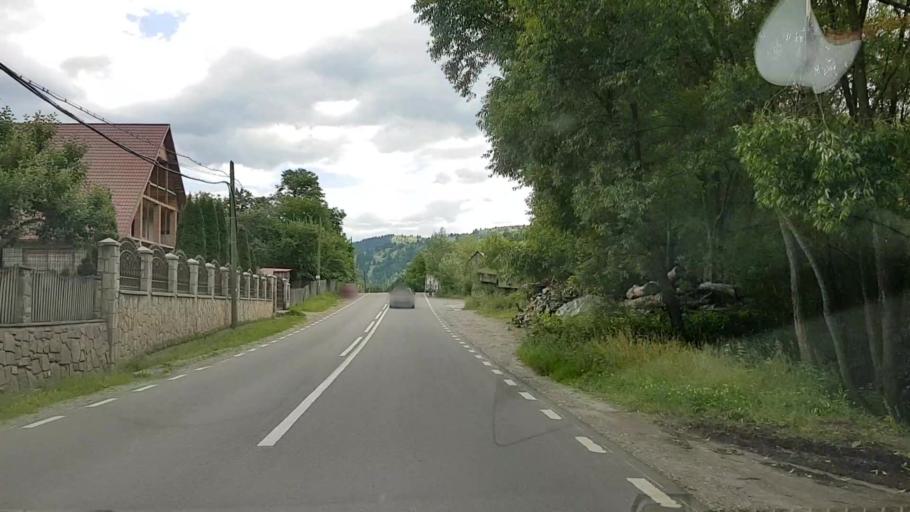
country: RO
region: Neamt
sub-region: Comuna Farcasa
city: Farcasa
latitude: 47.1680
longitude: 25.8037
